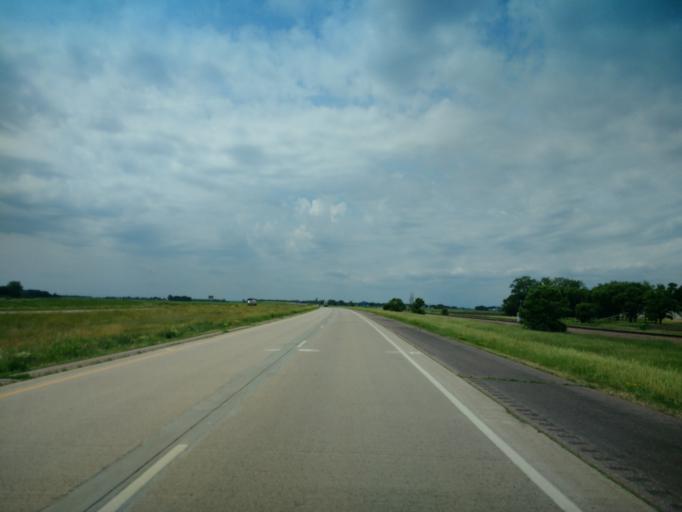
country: US
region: Minnesota
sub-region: Watonwan County
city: Saint James
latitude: 43.9635
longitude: -94.7513
